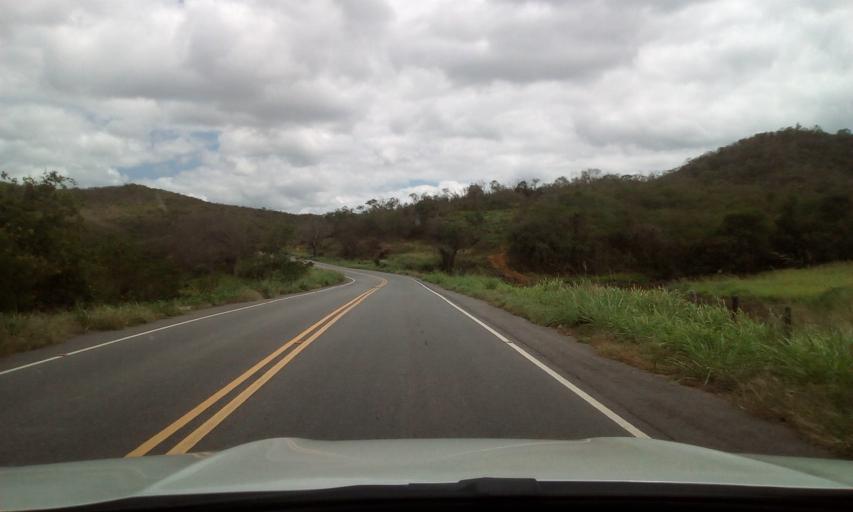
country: BR
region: Paraiba
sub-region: Serra Redonda
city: Alagoa Grande
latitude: -7.1490
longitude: -35.6136
